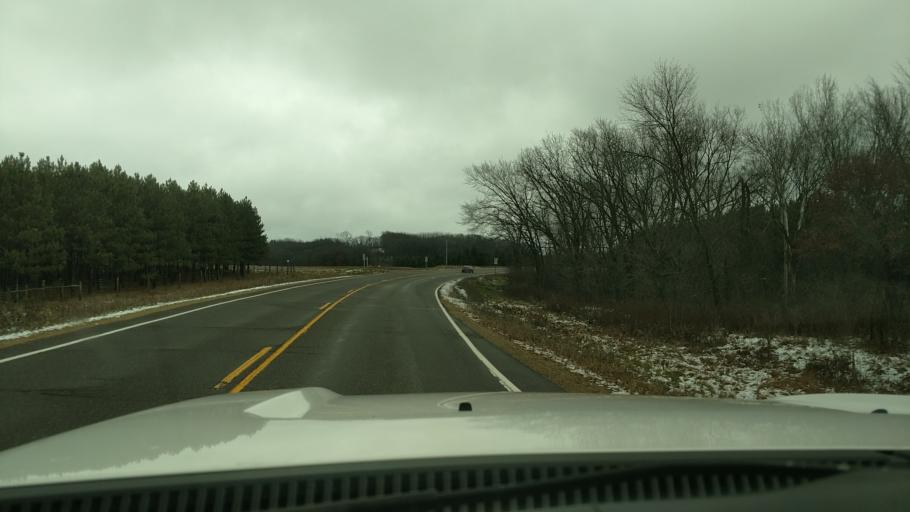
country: US
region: Wisconsin
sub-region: Dunn County
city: Boyceville
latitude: 45.1362
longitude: -91.9333
